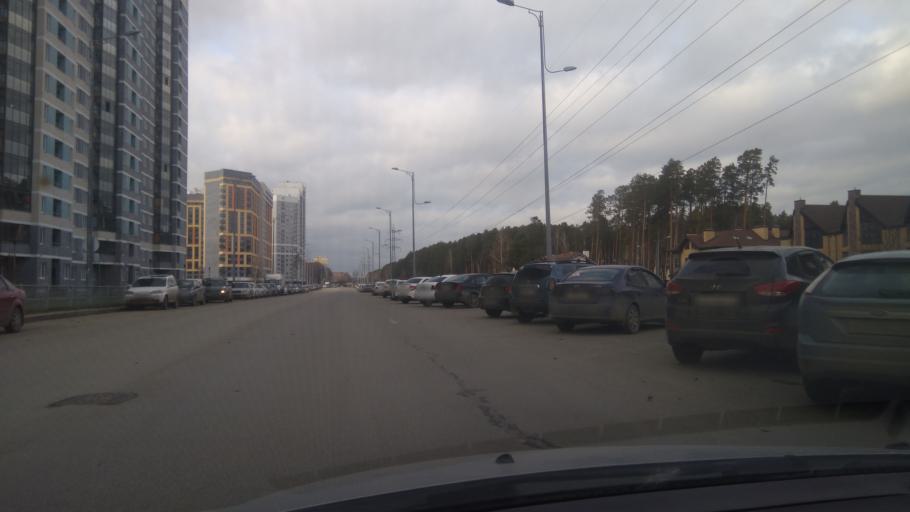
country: RU
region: Sverdlovsk
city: Sovkhoznyy
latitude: 56.7830
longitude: 60.5541
